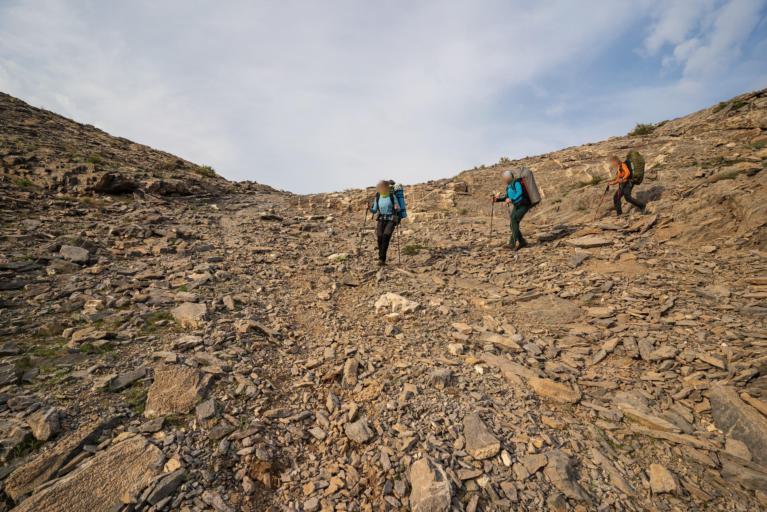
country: KZ
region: Ongtustik Qazaqstan
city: Ashchysay
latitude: 43.5756
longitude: 68.8859
